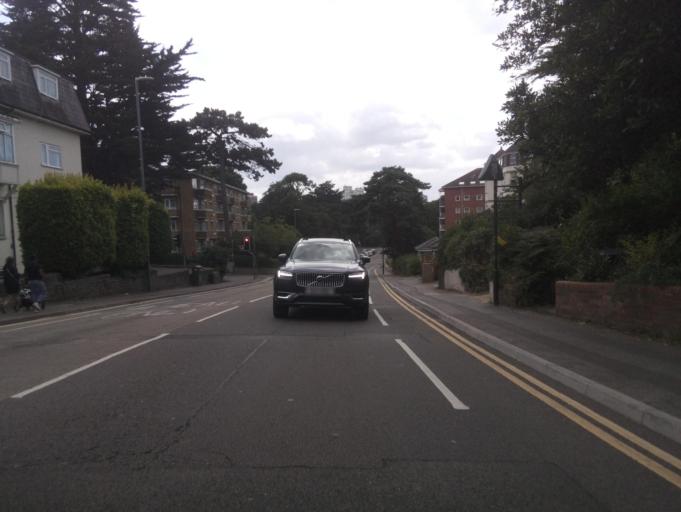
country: GB
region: England
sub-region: Bournemouth
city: Bournemouth
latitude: 50.7245
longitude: -1.8468
